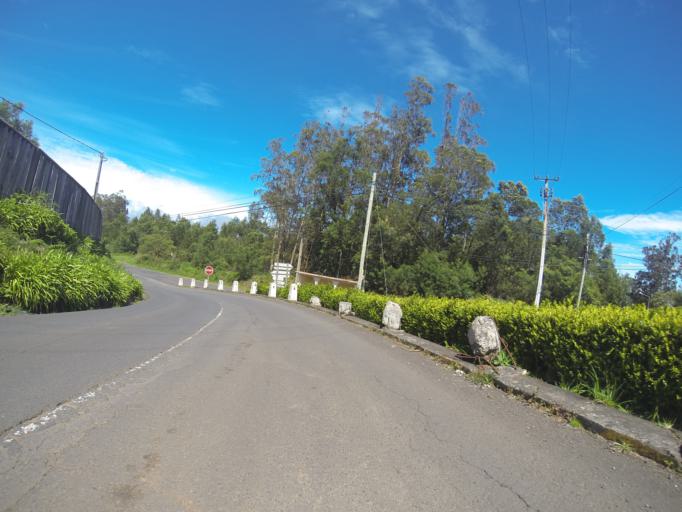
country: PT
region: Madeira
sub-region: Santa Cruz
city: Camacha
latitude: 32.7178
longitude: -16.8328
